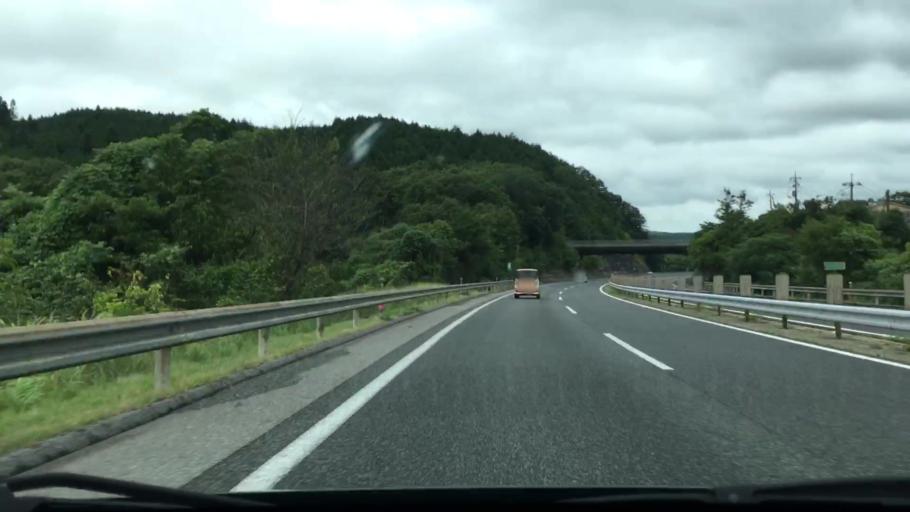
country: JP
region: Hiroshima
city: Miyoshi
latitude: 34.7733
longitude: 132.8338
